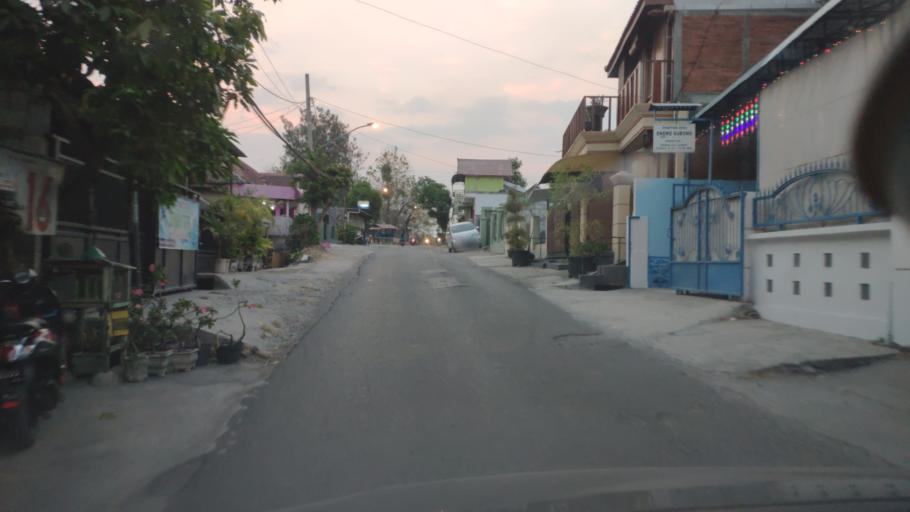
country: ID
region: Central Java
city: Cepu
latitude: -7.1489
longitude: 111.5883
